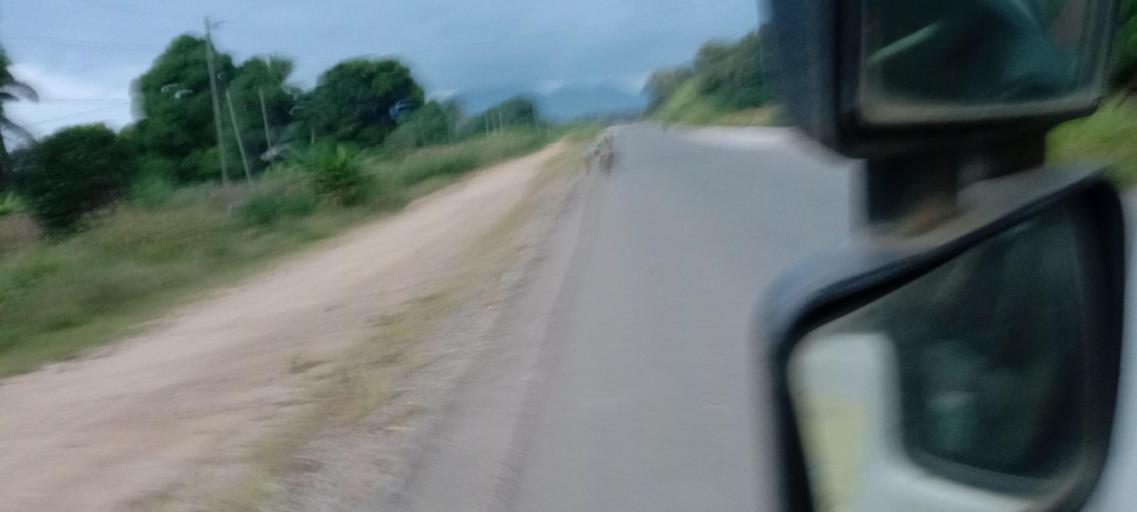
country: TZ
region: Morogoro
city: Ifakara
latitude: -7.9584
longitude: 36.8532
